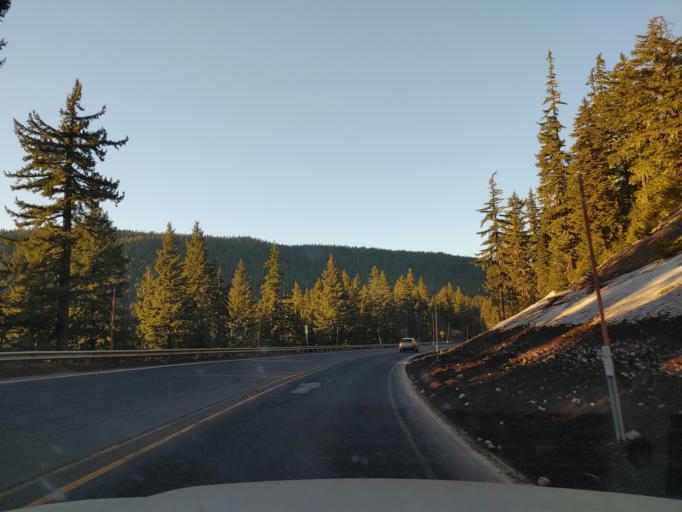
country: US
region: Oregon
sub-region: Lane County
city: Oakridge
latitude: 43.6155
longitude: -122.0697
